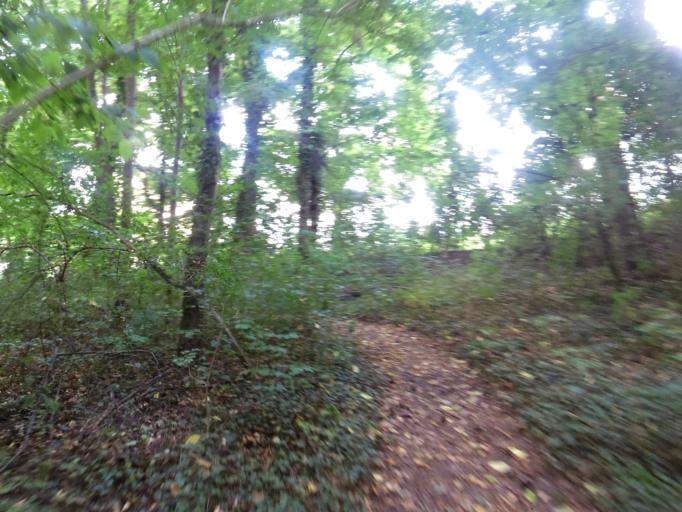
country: DE
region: Bavaria
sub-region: Regierungsbezirk Unterfranken
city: Randersacker
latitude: 49.7421
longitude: 9.9529
